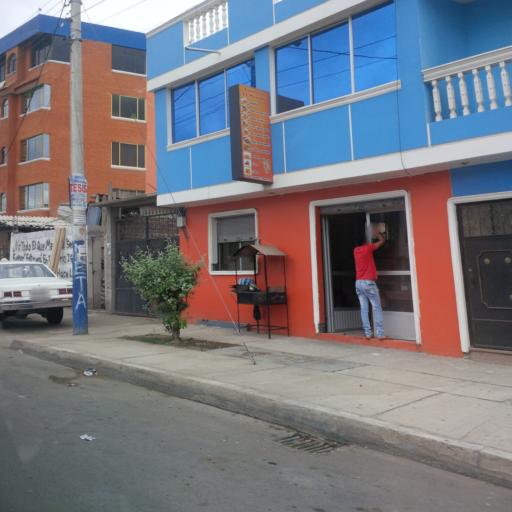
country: EC
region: Chimborazo
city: Riobamba
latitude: -1.6527
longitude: -78.6747
